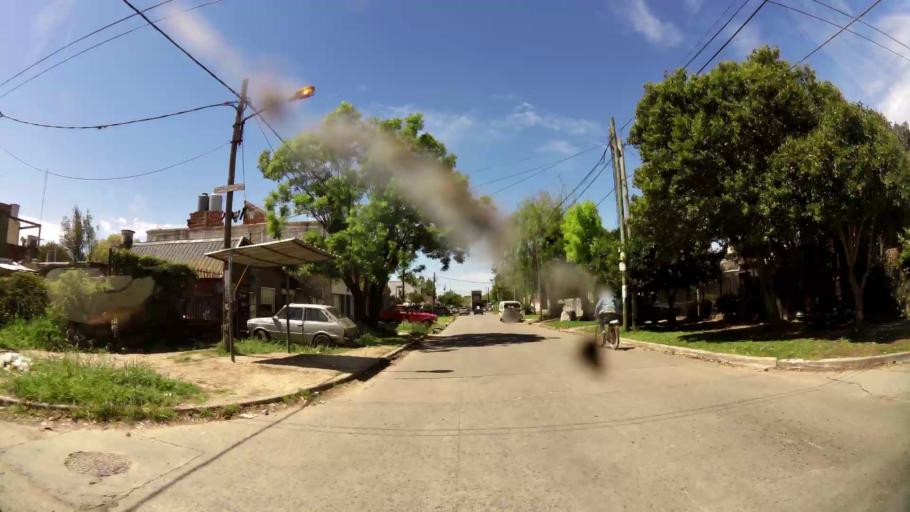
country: AR
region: Buenos Aires
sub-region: Partido de Quilmes
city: Quilmes
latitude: -34.7360
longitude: -58.3019
